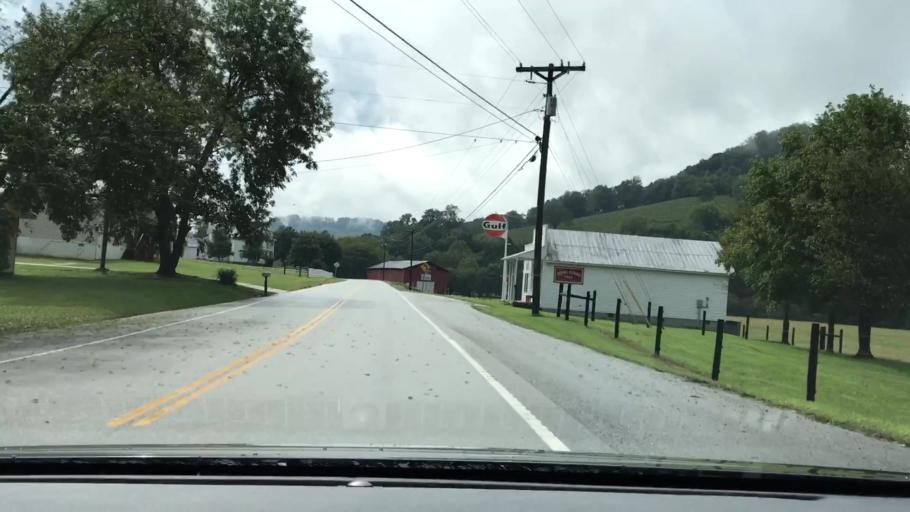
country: US
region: Tennessee
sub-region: Smith County
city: Carthage
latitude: 36.3510
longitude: -85.9639
